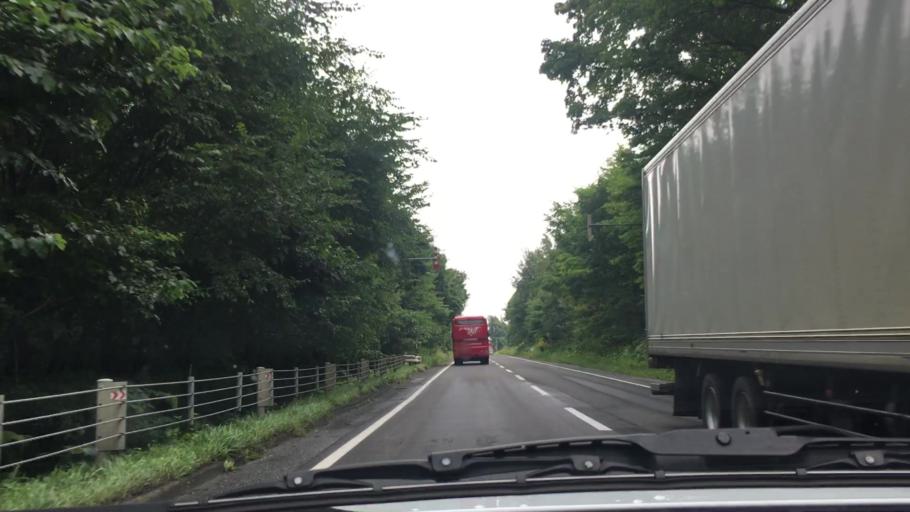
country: JP
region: Hokkaido
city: Chitose
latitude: 42.9431
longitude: 141.7523
